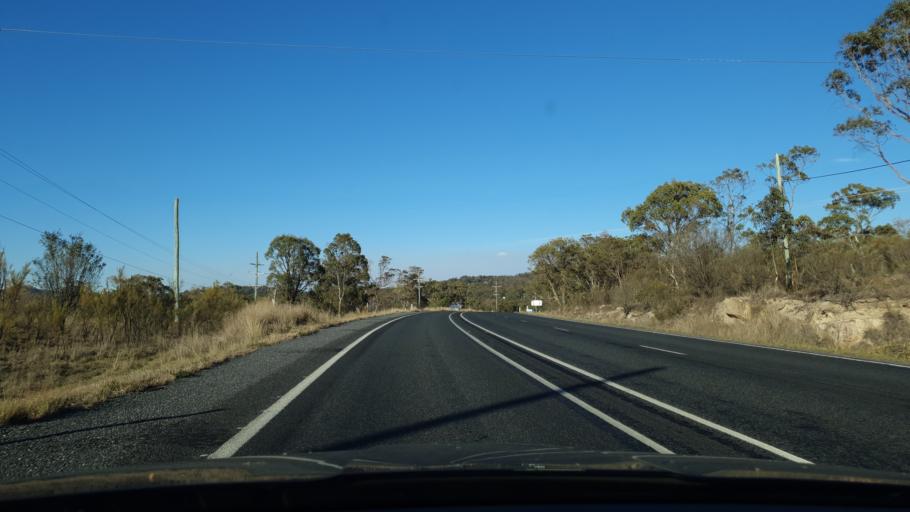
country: AU
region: Queensland
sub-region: Southern Downs
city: Stanthorpe
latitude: -28.6862
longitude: 151.9126
